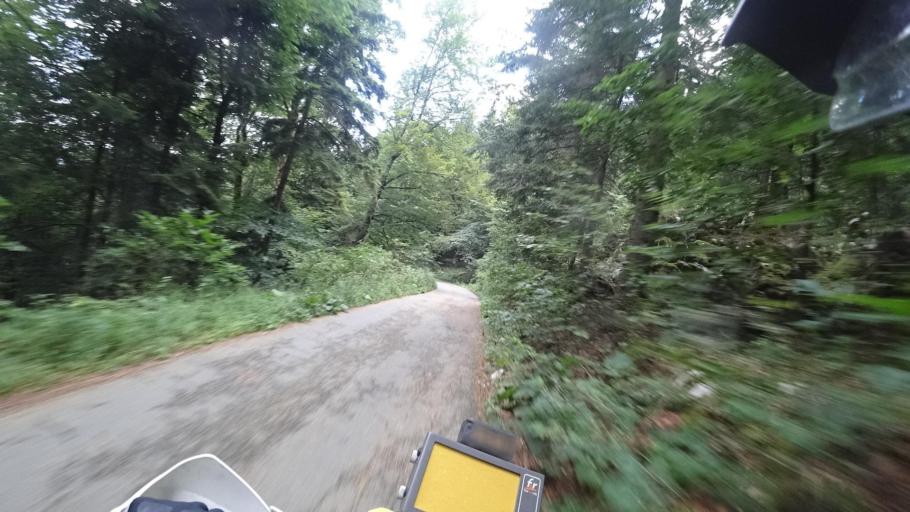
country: HR
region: Licko-Senjska
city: Senj
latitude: 45.1051
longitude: 14.9673
